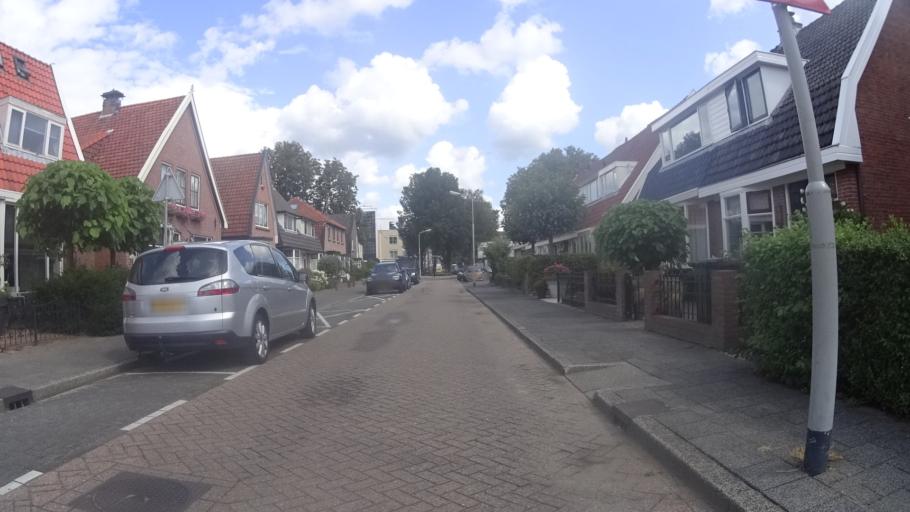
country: NL
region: North Holland
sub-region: Gemeente Beverwijk
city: Beverwijk
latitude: 52.4878
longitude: 4.6469
